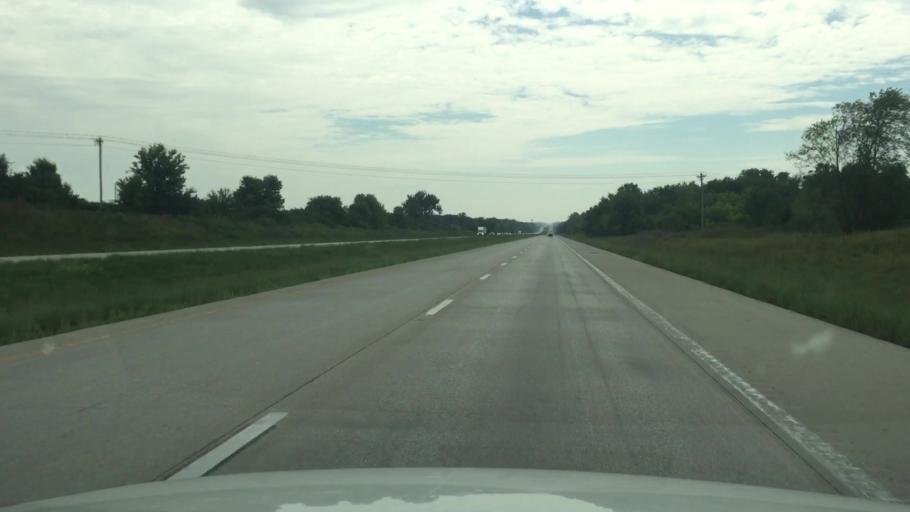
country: US
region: Missouri
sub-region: Clay County
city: Kearney
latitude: 39.4053
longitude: -94.3524
